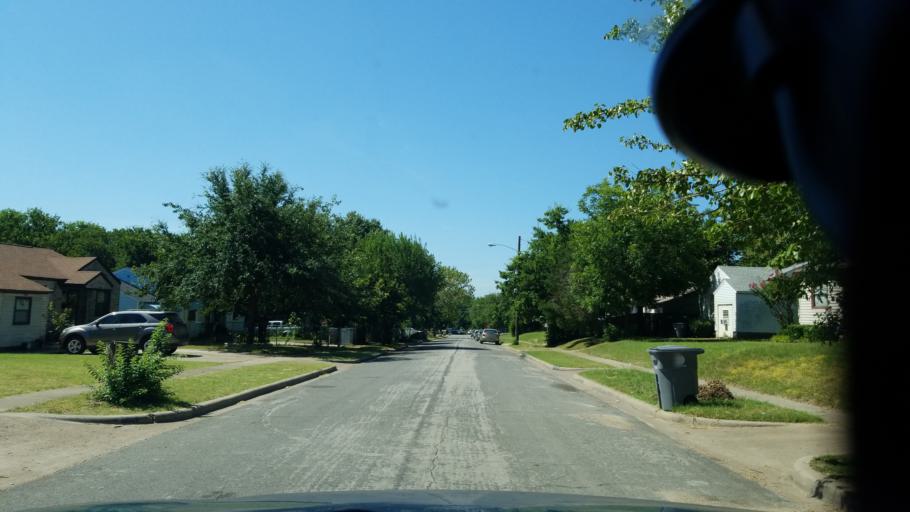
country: US
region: Texas
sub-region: Dallas County
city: Cockrell Hill
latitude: 32.7048
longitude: -96.8183
